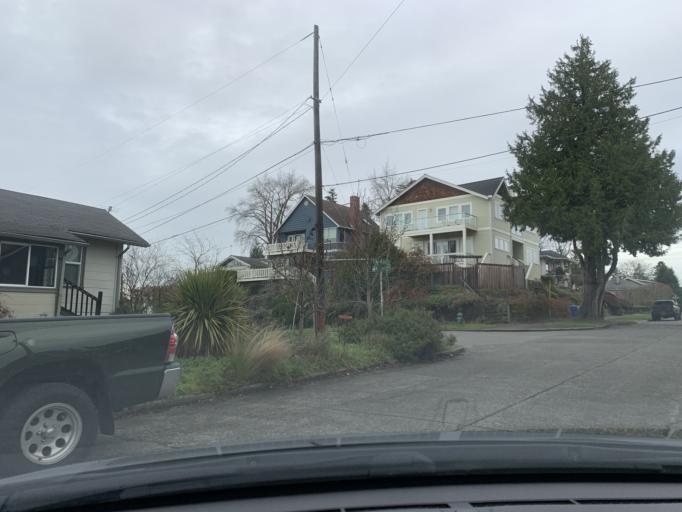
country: US
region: Washington
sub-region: King County
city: White Center
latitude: 47.5540
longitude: -122.3909
